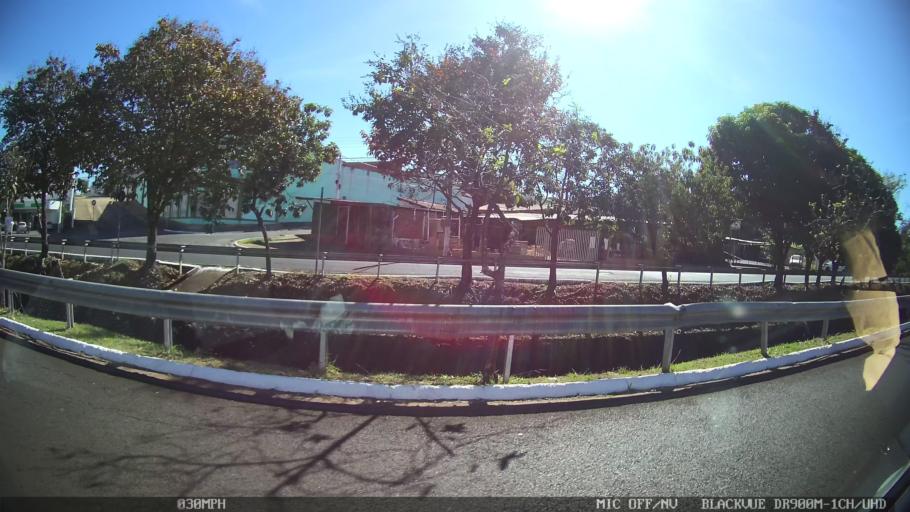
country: BR
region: Sao Paulo
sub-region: Franca
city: Franca
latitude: -20.5199
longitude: -47.3877
